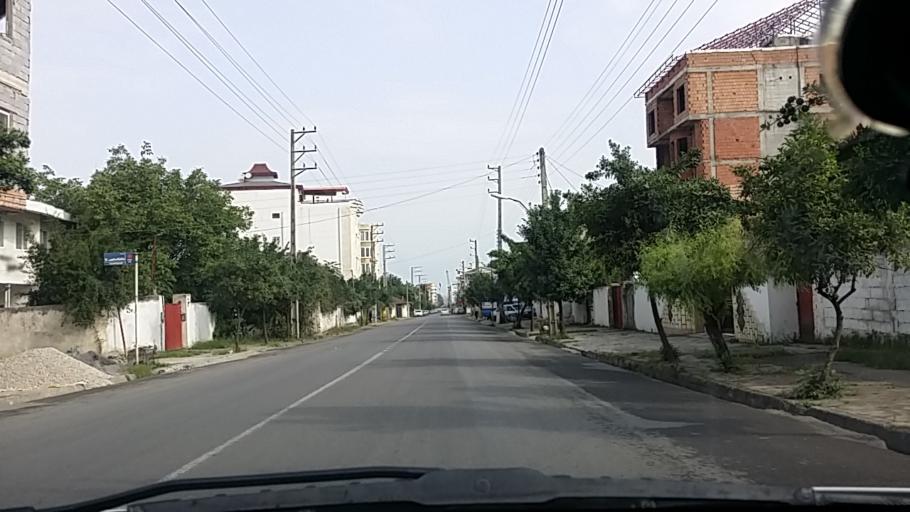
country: IR
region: Mazandaran
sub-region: Nowshahr
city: Nowshahr
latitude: 36.6415
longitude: 51.5082
